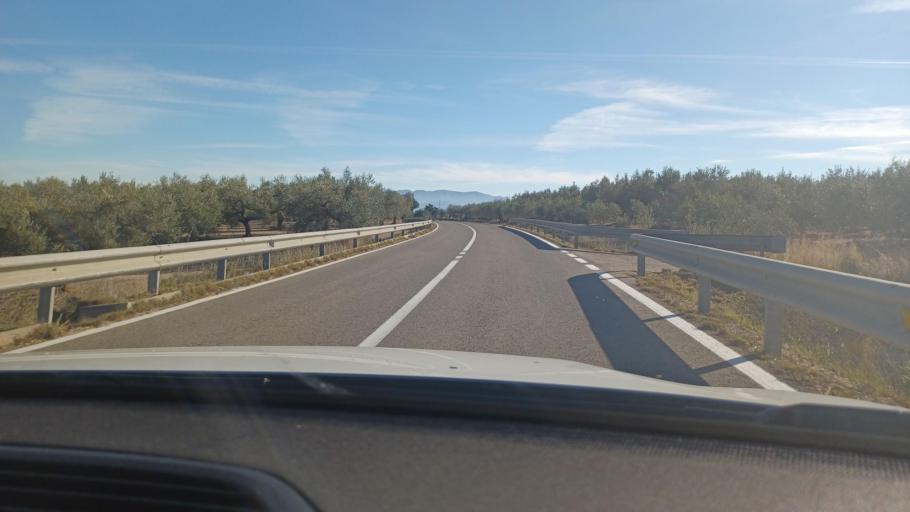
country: ES
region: Catalonia
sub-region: Provincia de Tarragona
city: Mas de Barberans
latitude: 40.7204
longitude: 0.3971
